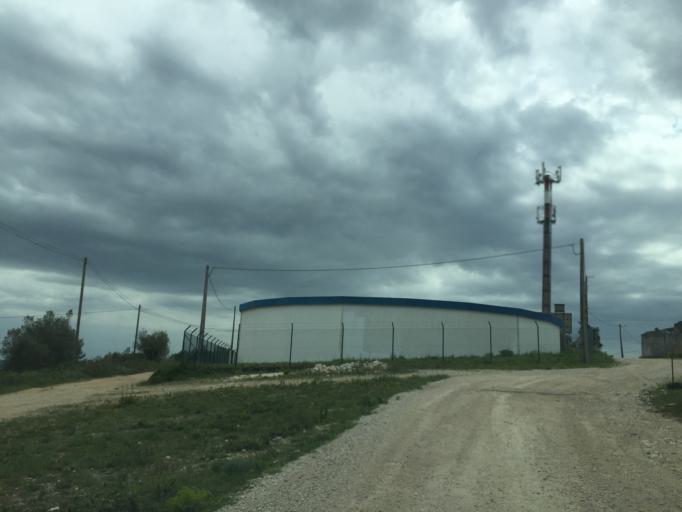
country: PT
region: Leiria
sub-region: Leiria
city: Santa Catarina da Serra
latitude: 39.6447
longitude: -8.6803
